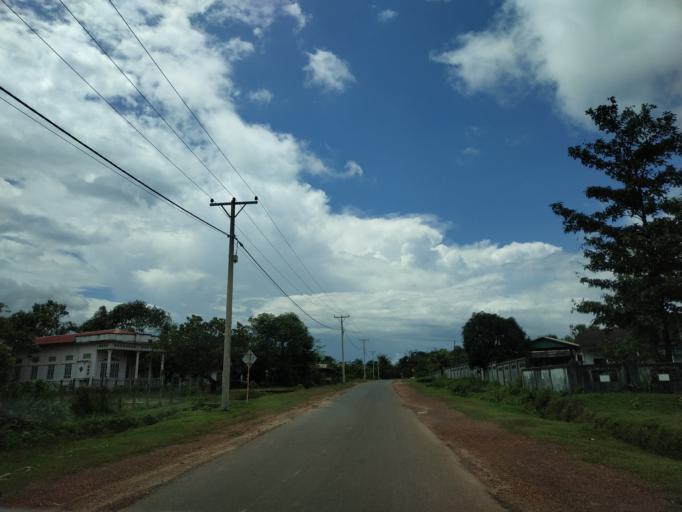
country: MM
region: Tanintharyi
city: Dawei
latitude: 14.1828
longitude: 98.1643
